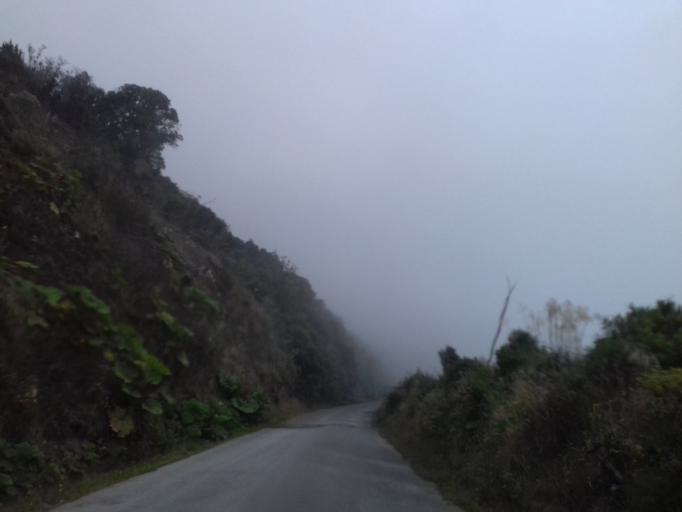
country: CO
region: Tolima
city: Herveo
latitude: 5.0074
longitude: -75.3279
